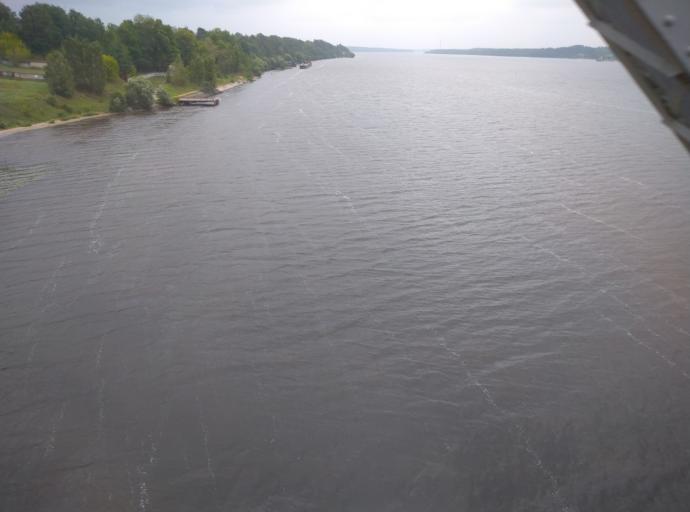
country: RU
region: Kostroma
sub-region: Kostromskoy Rayon
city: Kostroma
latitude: 57.7402
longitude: 40.9594
